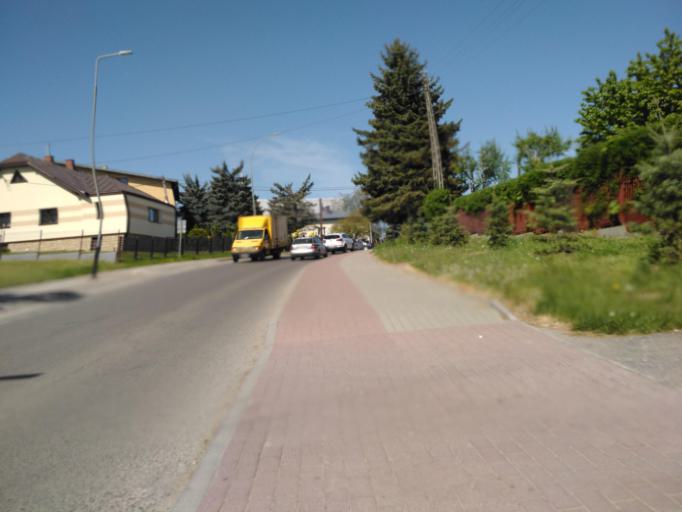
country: PL
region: Subcarpathian Voivodeship
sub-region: Krosno
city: Krosno
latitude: 49.6814
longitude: 21.7866
